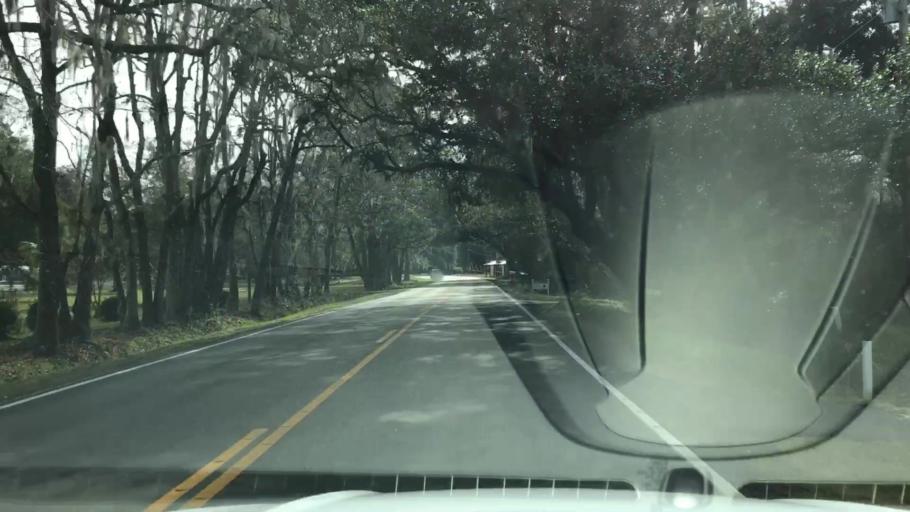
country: US
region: South Carolina
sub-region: Charleston County
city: Shell Point
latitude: 32.7338
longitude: -80.0310
